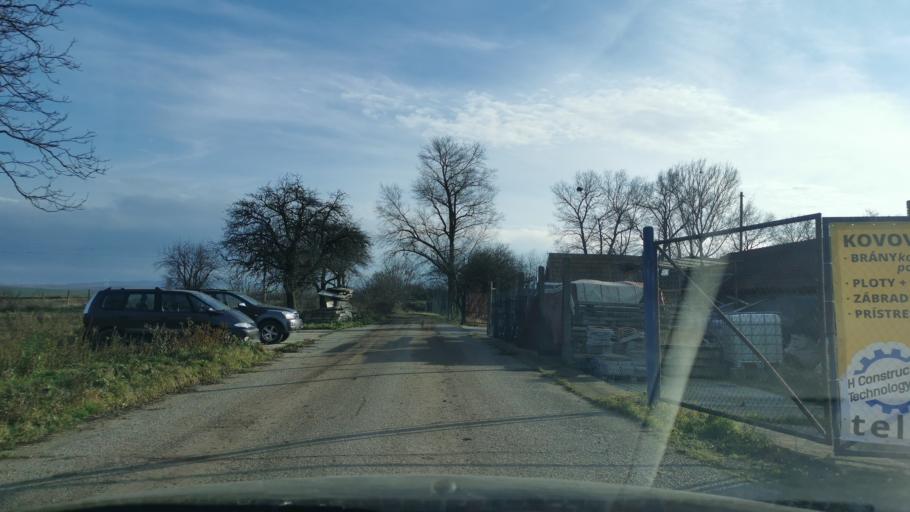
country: SK
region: Trnavsky
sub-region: Okres Skalica
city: Holic
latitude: 48.7872
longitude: 17.1295
